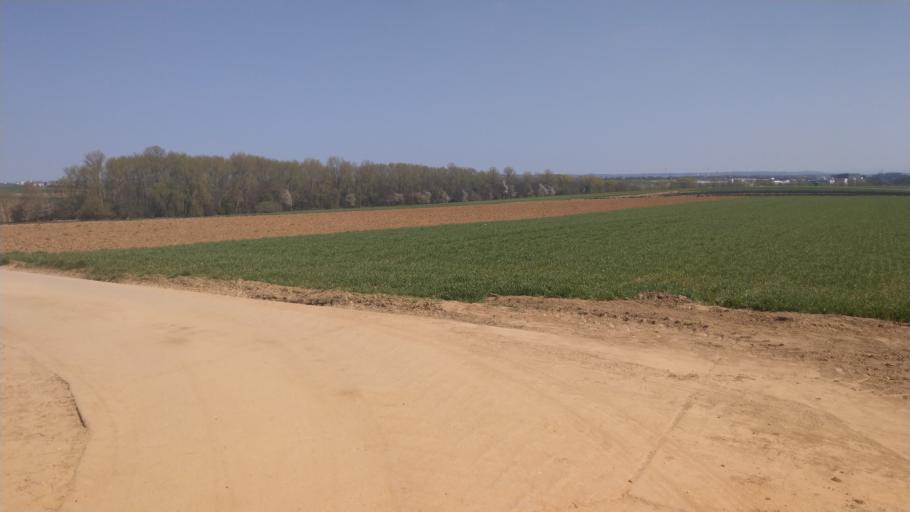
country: DE
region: Baden-Wuerttemberg
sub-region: Regierungsbezirk Stuttgart
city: Neuhausen auf den Fildern
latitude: 48.6873
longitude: 9.2465
